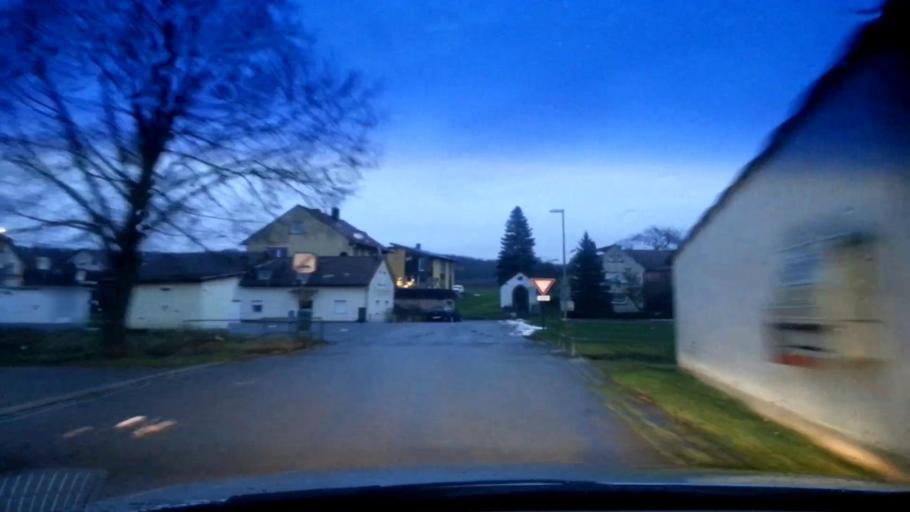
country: DE
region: Bavaria
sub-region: Upper Franconia
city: Schesslitz
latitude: 49.9733
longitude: 10.9861
